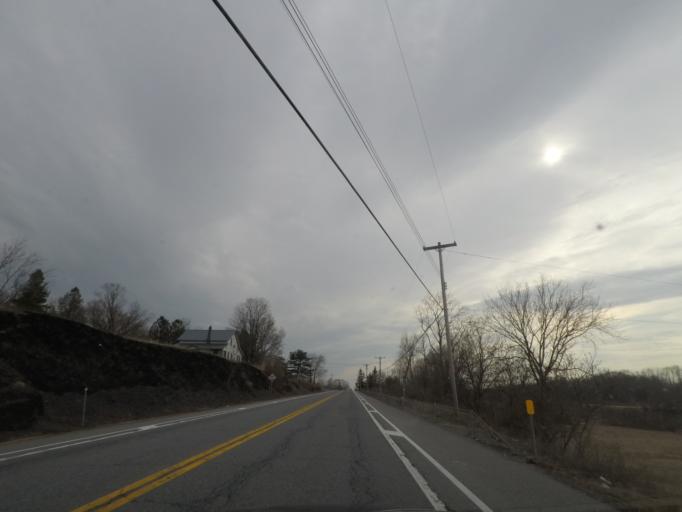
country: US
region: New York
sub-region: Washington County
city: Fort Edward
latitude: 43.2072
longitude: -73.5783
